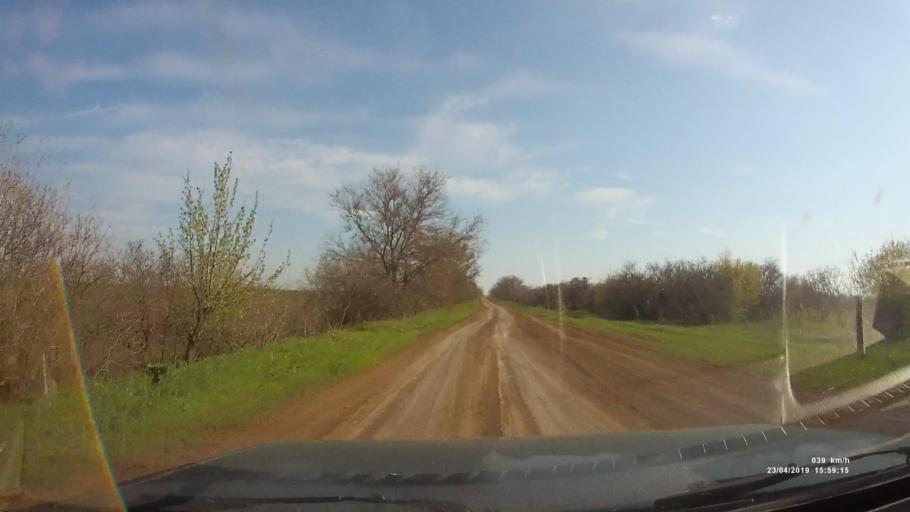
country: RU
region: Rostov
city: Remontnoye
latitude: 46.5181
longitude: 43.1096
